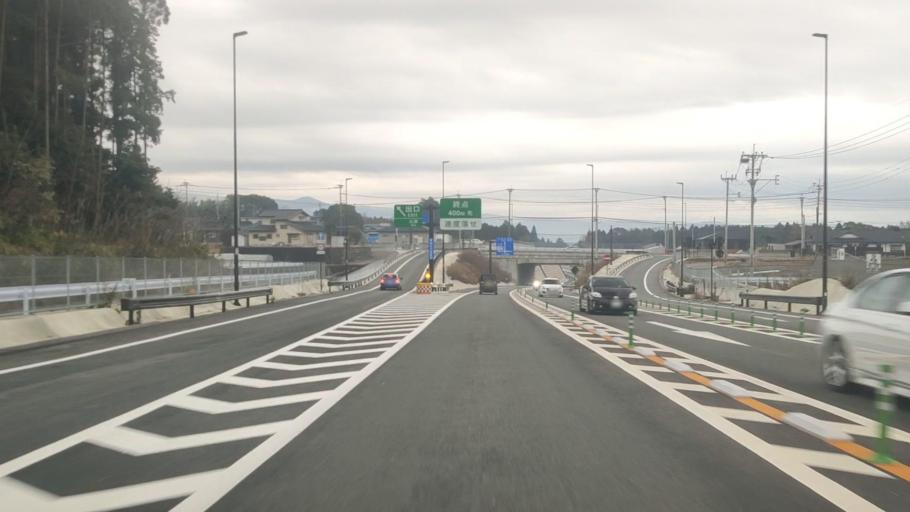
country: JP
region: Kumamoto
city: Ozu
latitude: 32.8918
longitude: 130.8962
